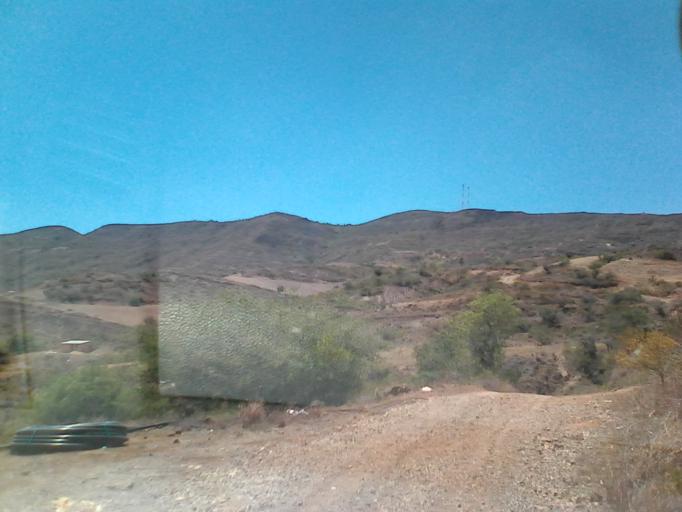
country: CO
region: Boyaca
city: Sachica
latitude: 5.6004
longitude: -73.5666
